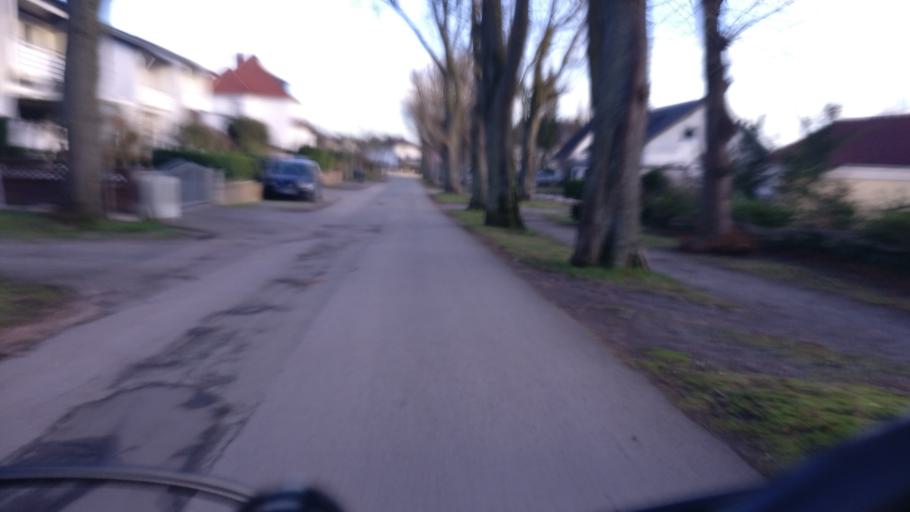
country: DE
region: North Rhine-Westphalia
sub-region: Regierungsbezirk Detmold
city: Lage
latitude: 51.9982
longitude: 8.7916
